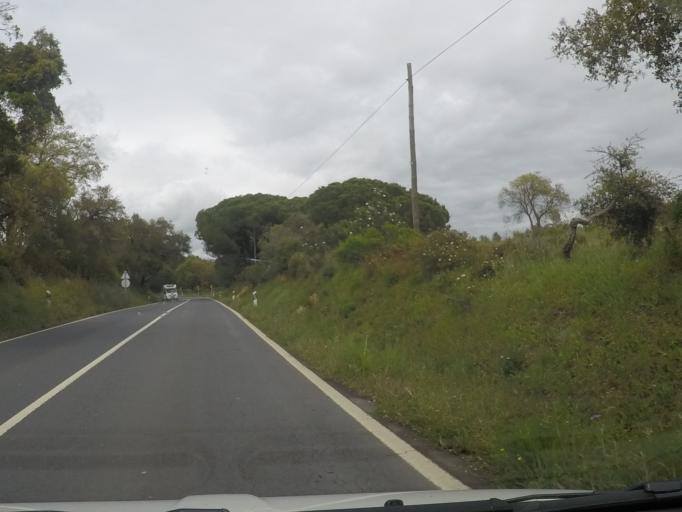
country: PT
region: Setubal
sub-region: Sines
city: Porto Covo
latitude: 37.8725
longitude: -8.7432
